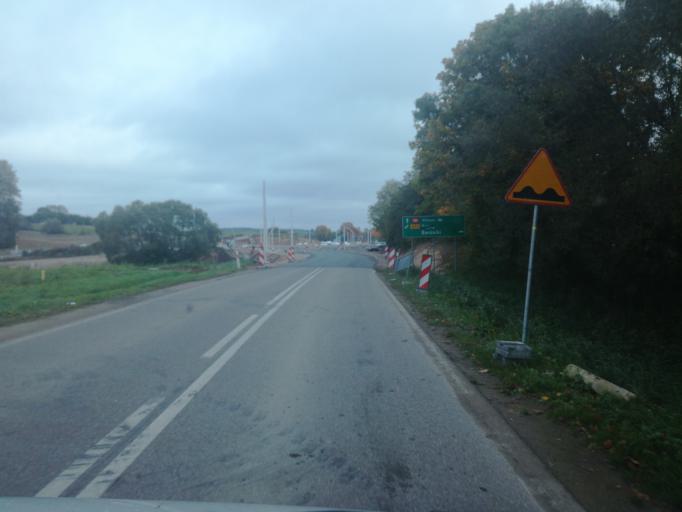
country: PL
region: Podlasie
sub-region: Powiat sejnenski
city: Sejny
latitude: 54.1055
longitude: 23.4086
